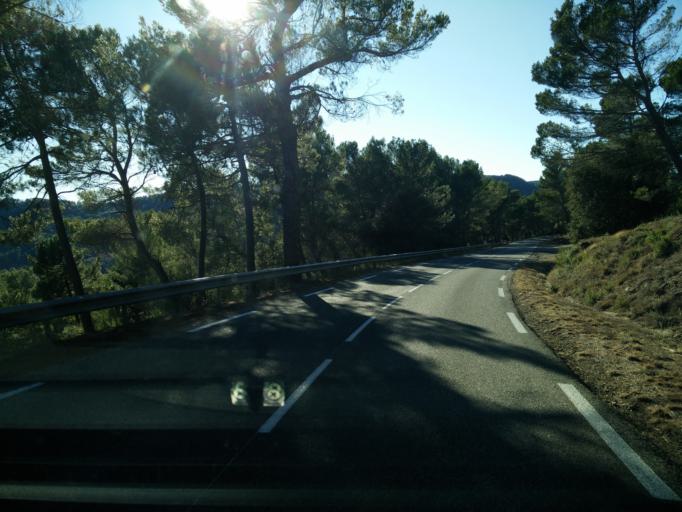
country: FR
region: Provence-Alpes-Cote d'Azur
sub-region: Departement du Var
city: Salernes
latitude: 43.5755
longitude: 6.2207
